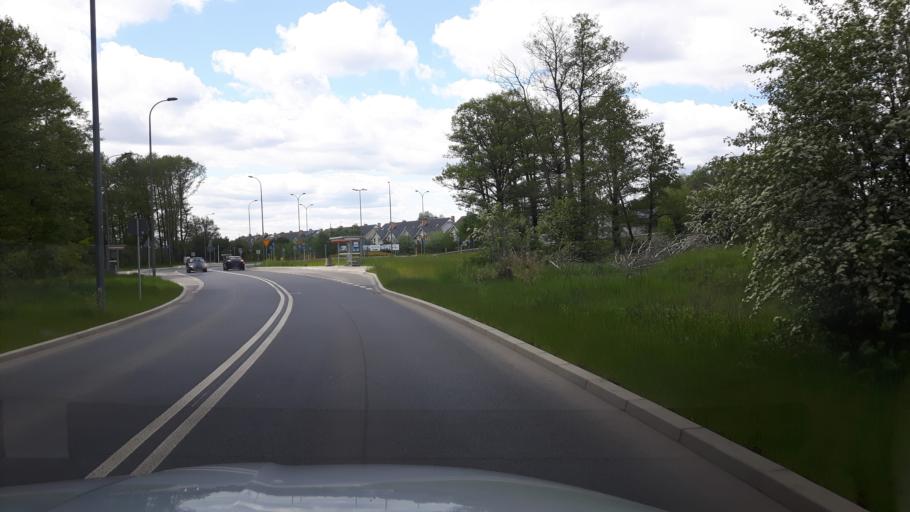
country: PL
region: Masovian Voivodeship
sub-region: Powiat legionowski
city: Stanislawow Pierwszy
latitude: 52.3399
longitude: 21.0523
